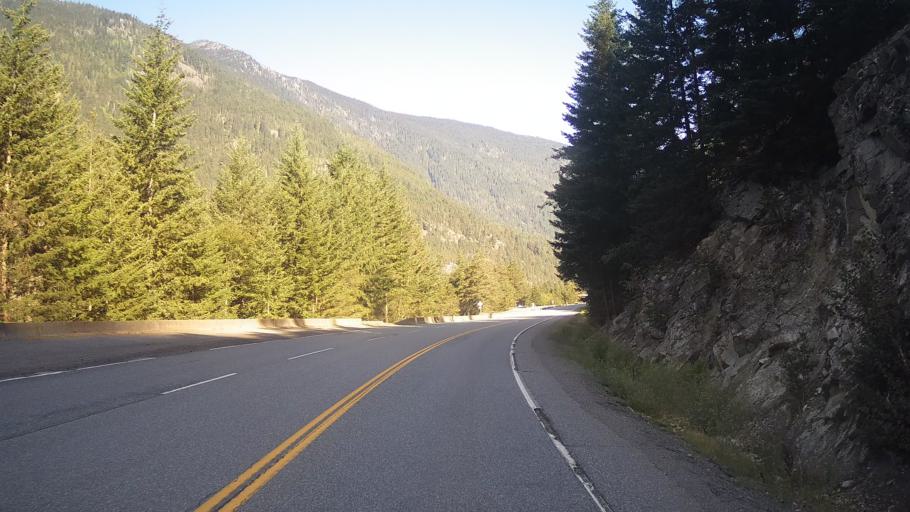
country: CA
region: British Columbia
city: Hope
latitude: 49.7750
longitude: -121.4389
